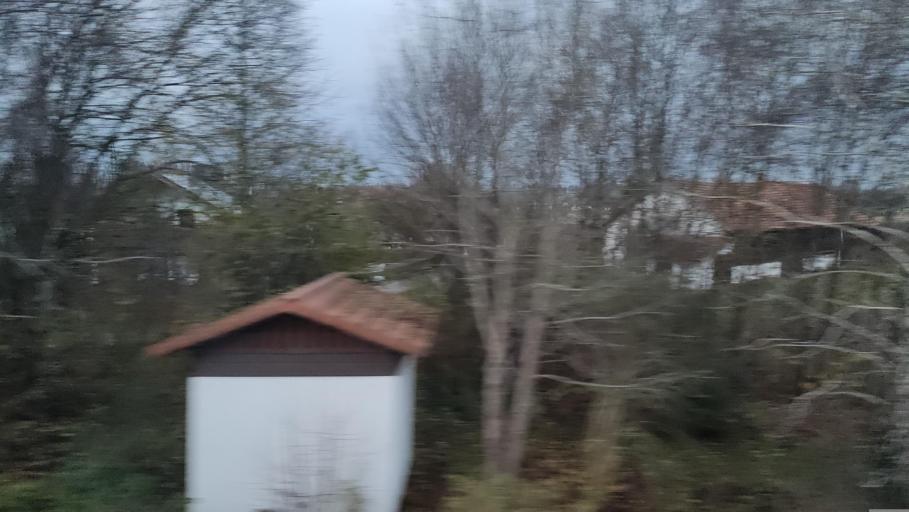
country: DE
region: Bavaria
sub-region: Upper Bavaria
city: Rattenkirchen
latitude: 48.2552
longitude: 12.3448
